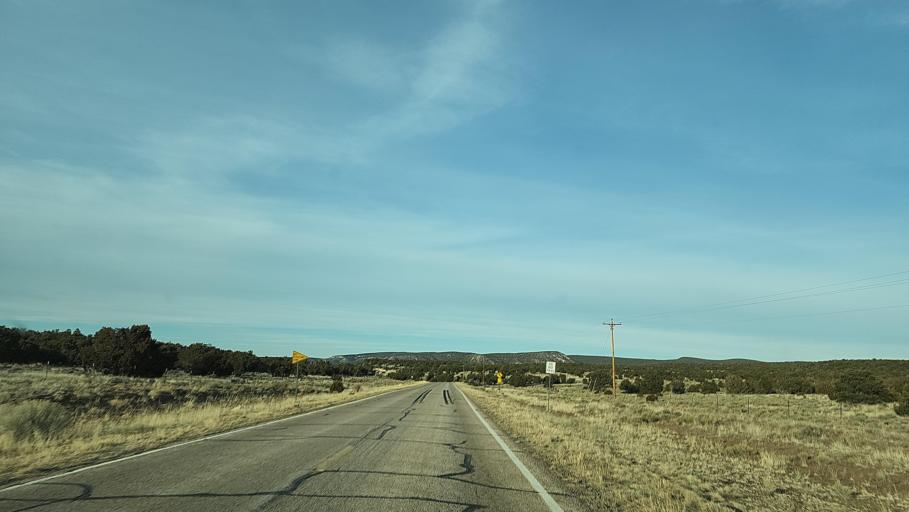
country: US
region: New Mexico
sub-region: McKinley County
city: Black Rock
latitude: 34.4135
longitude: -108.4329
